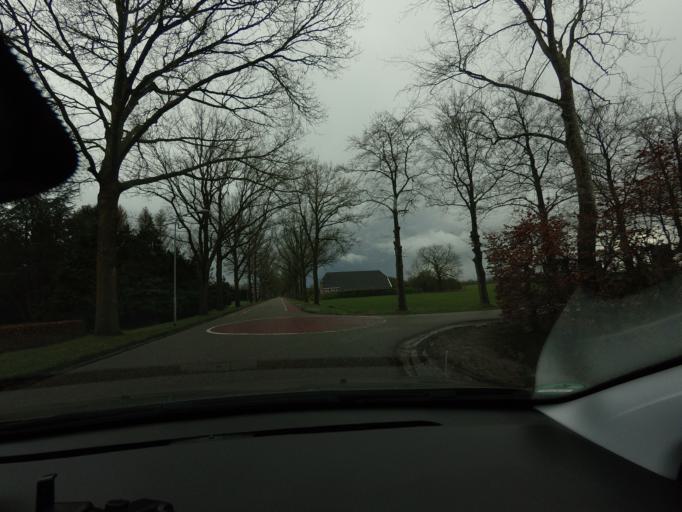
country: NL
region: Drenthe
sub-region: Gemeente Borger-Odoorn
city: Borger
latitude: 52.9847
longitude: 6.7824
